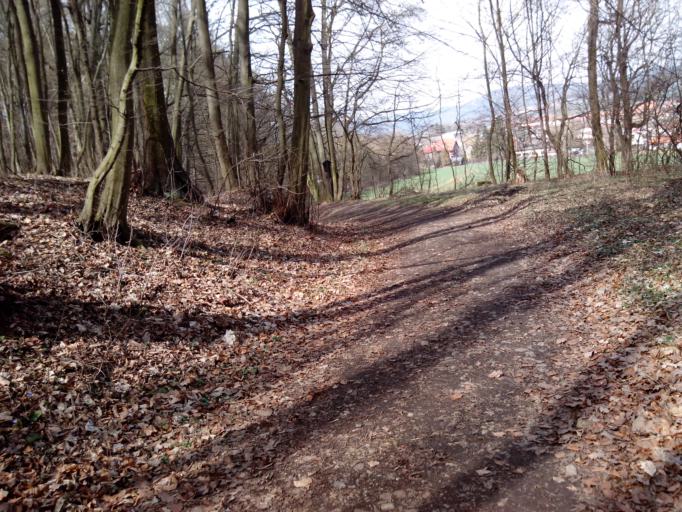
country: CZ
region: Central Bohemia
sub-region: Okres Beroun
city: Beroun
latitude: 49.9426
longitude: 14.1029
